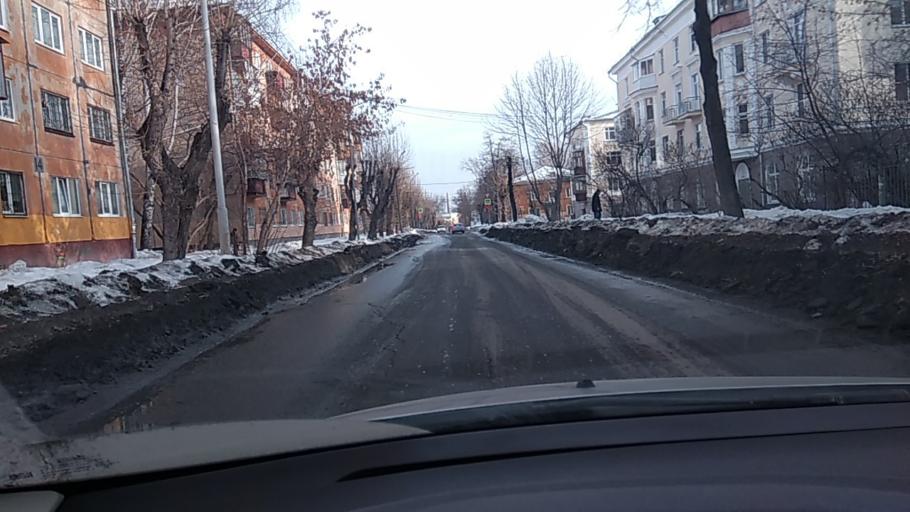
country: RU
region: Sverdlovsk
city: Yekaterinburg
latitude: 56.8881
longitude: 60.5761
